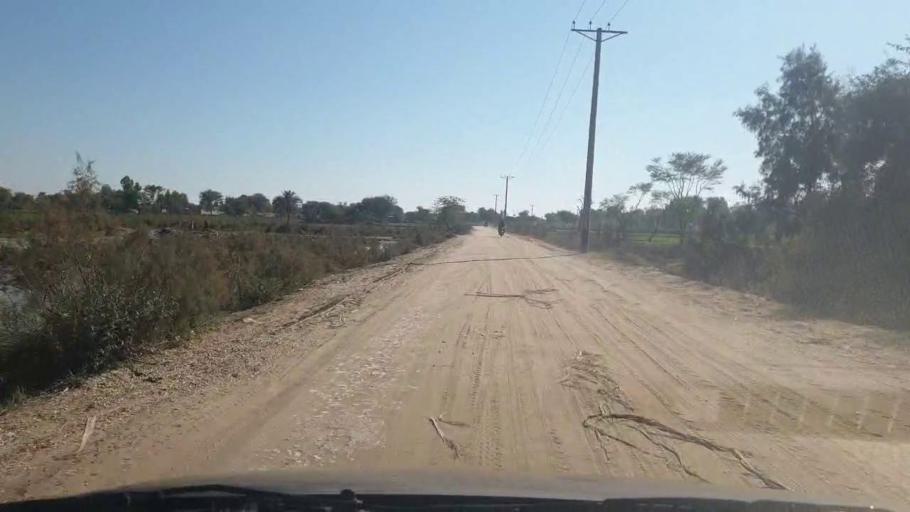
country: PK
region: Sindh
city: Bozdar
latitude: 27.0737
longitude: 68.6166
